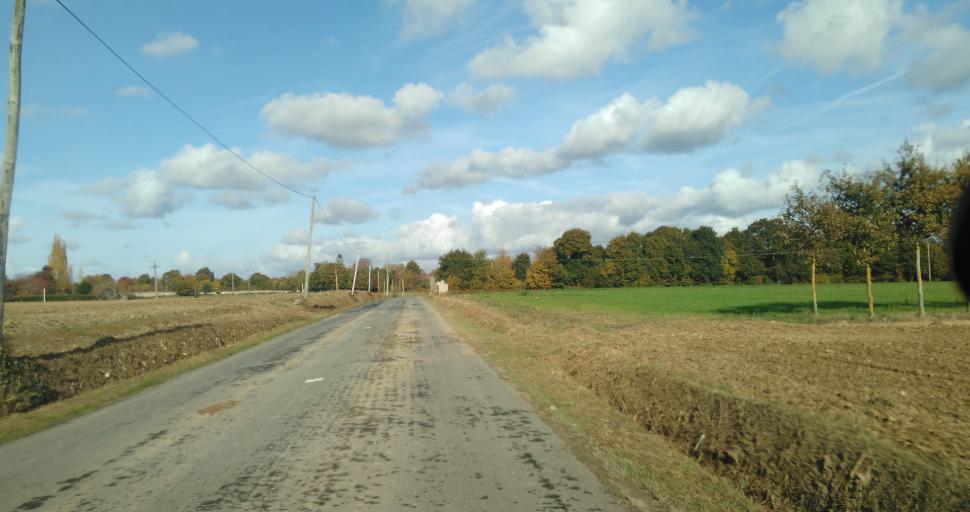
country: FR
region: Brittany
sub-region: Departement d'Ille-et-Vilaine
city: Boisgervilly
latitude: 48.1559
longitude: -2.0705
